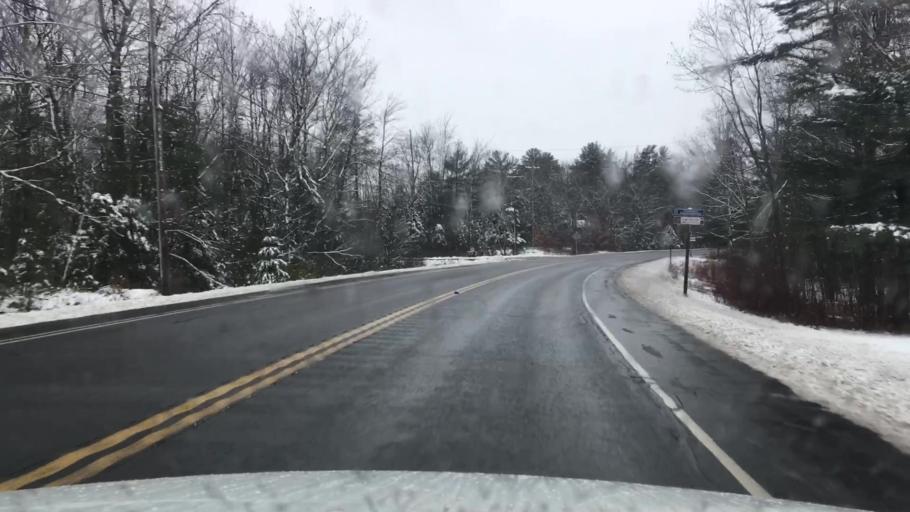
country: US
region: Maine
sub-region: Knox County
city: Rockport
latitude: 44.1783
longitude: -69.1304
